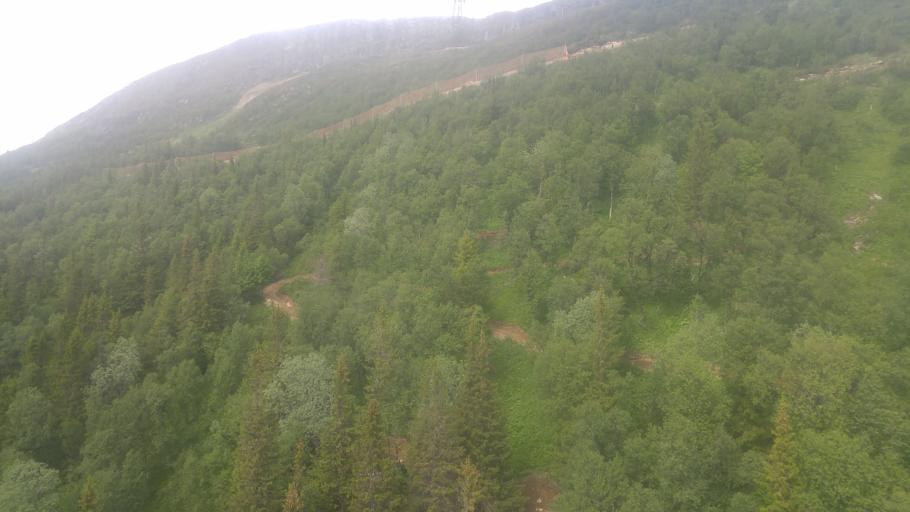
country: SE
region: Jaemtland
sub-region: Are Kommun
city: Are
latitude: 63.4100
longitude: 13.0772
